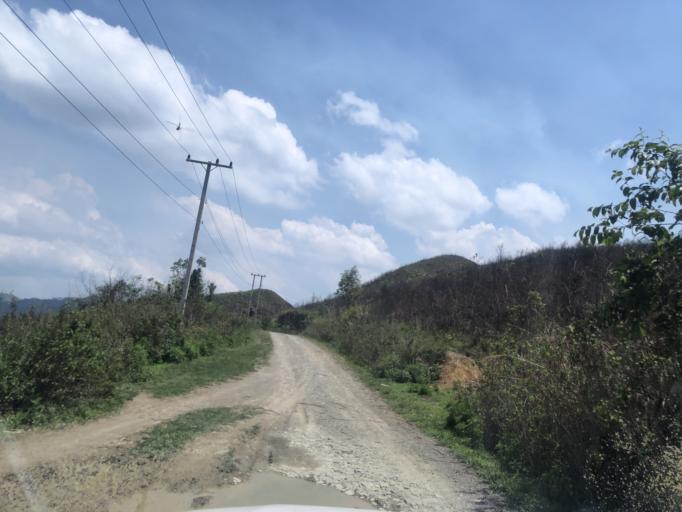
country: LA
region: Phongsali
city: Phongsali
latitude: 21.4143
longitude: 102.1859
